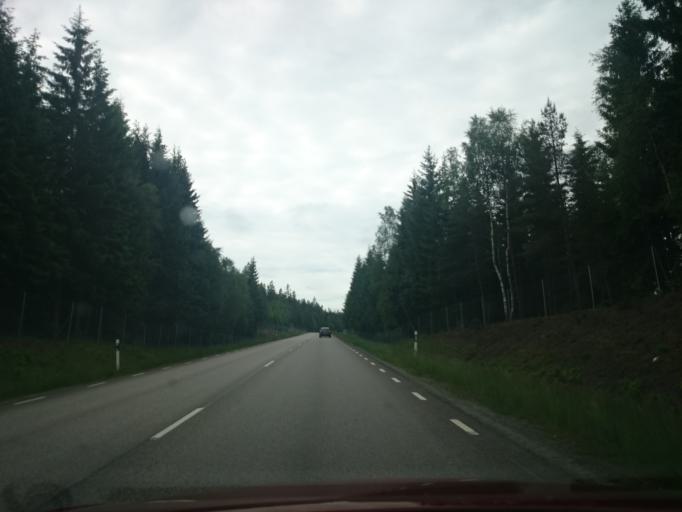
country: SE
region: Vaestra Goetaland
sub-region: Harryda Kommun
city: Hindas
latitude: 57.6904
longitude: 12.3724
